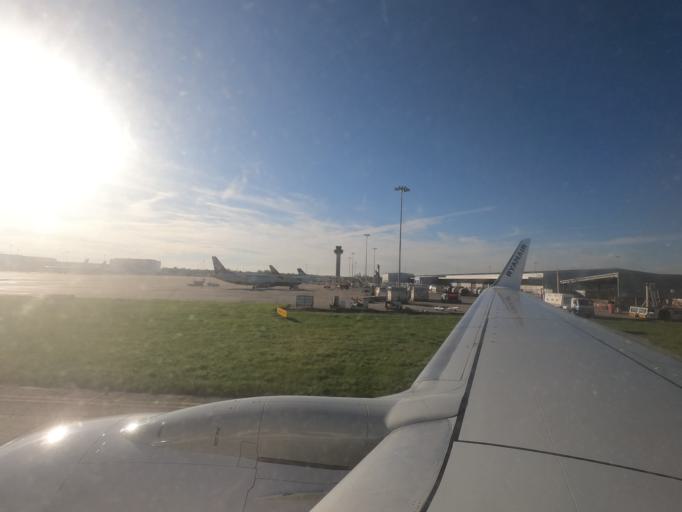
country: GB
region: England
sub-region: Essex
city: Takeley
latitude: 51.8889
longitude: 0.2484
